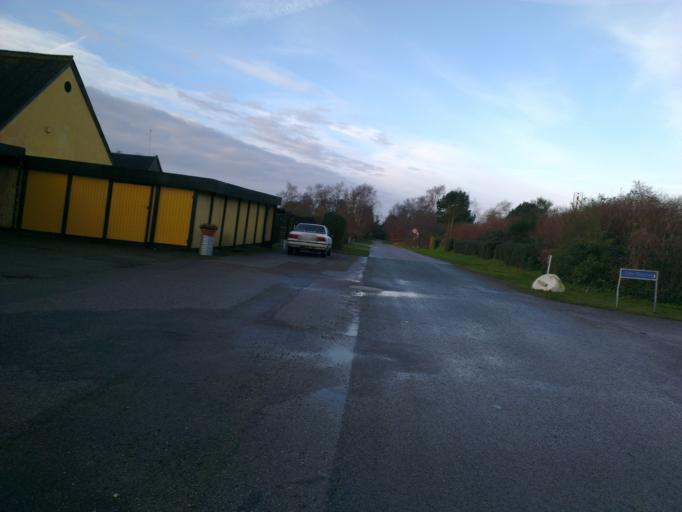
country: DK
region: Capital Region
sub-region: Frederikssund Kommune
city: Jaegerspris
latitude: 55.8398
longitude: 11.9616
